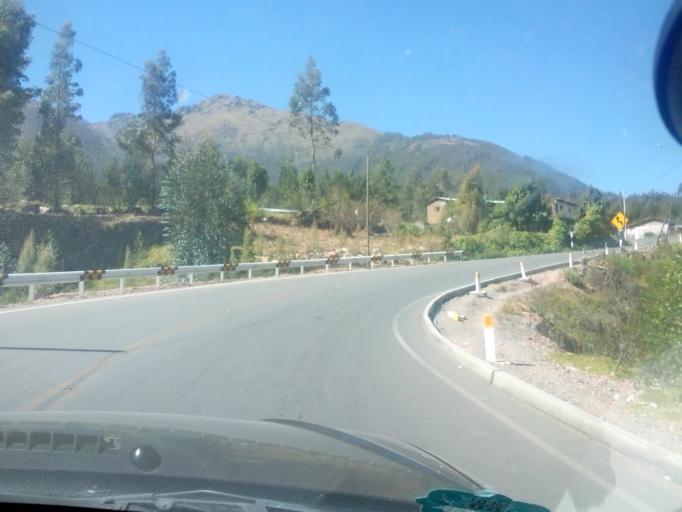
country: PE
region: Apurimac
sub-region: Chincheros
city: Chincheros
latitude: -13.5152
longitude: -73.7068
